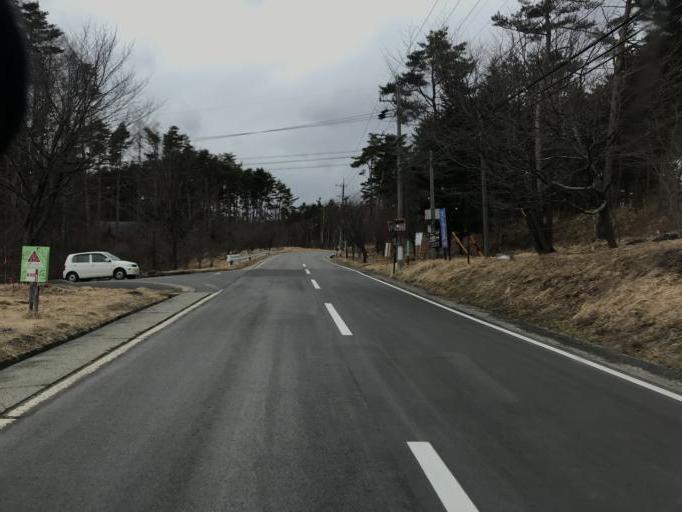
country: JP
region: Nagano
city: Chino
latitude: 35.9258
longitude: 138.2974
